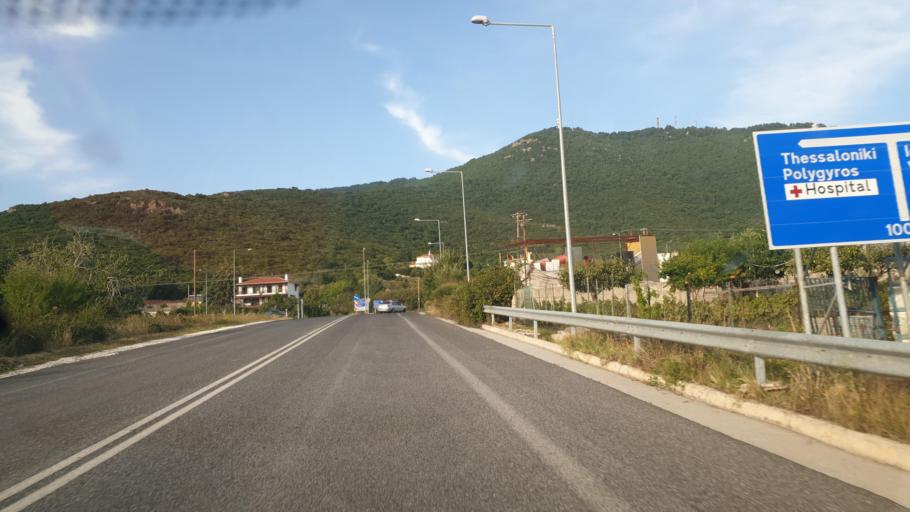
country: GR
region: Central Macedonia
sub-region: Nomos Chalkidikis
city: Polygyros
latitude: 40.3730
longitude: 23.4530
